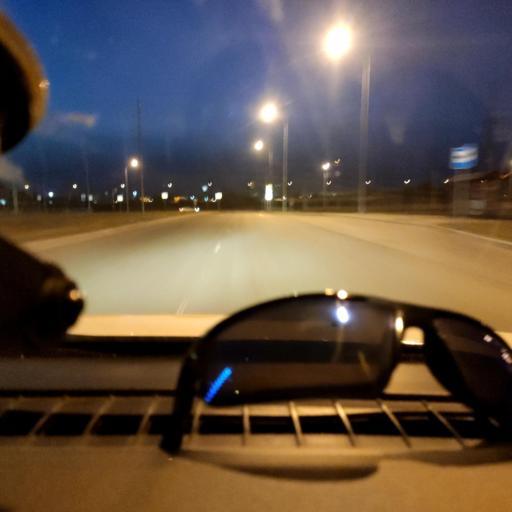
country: RU
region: Samara
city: Samara
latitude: 53.0980
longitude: 50.1646
